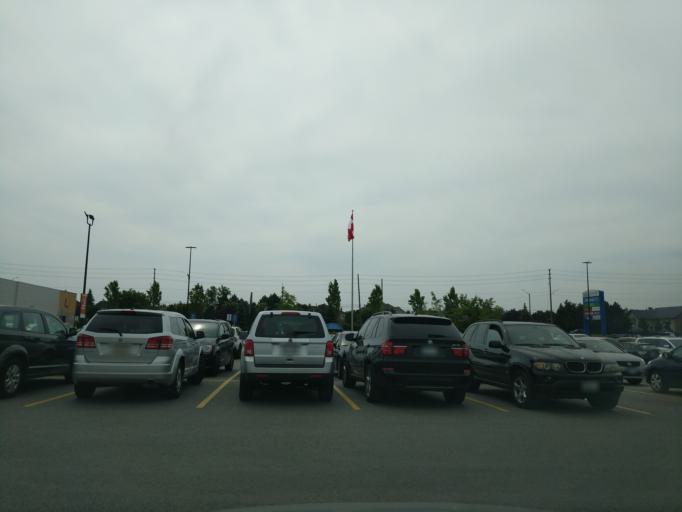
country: CA
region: Ontario
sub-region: York
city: Richmond Hill
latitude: 43.8775
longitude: -79.4096
